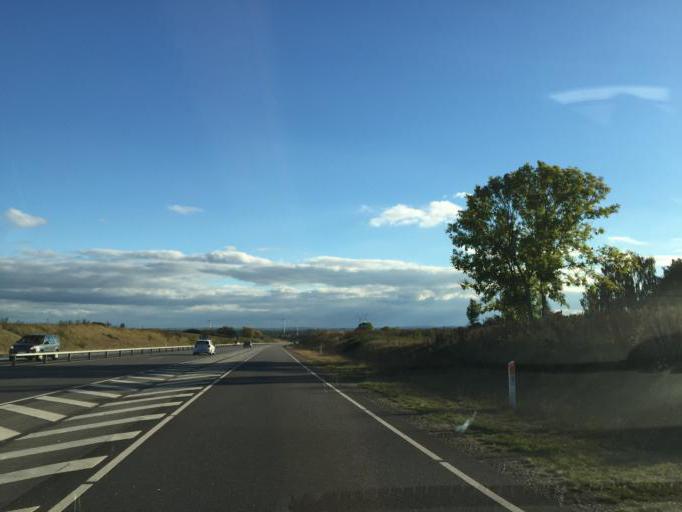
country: DK
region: Zealand
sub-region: Odsherred Kommune
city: Asnaes
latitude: 55.7908
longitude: 11.5828
